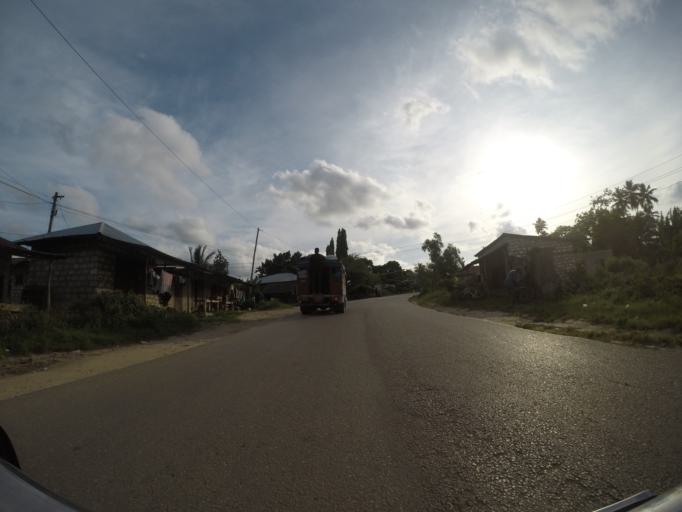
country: TZ
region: Pemba South
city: Chake Chake
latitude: -5.2624
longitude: 39.7738
